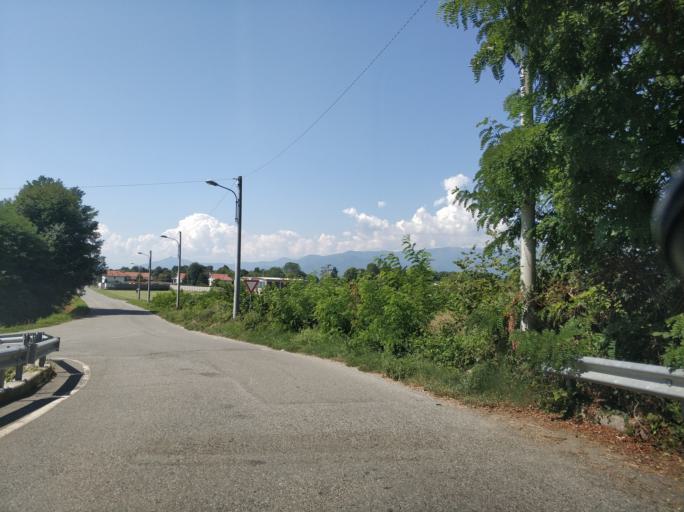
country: IT
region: Piedmont
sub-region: Provincia di Torino
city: San Maurizio
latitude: 45.2302
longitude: 7.6382
